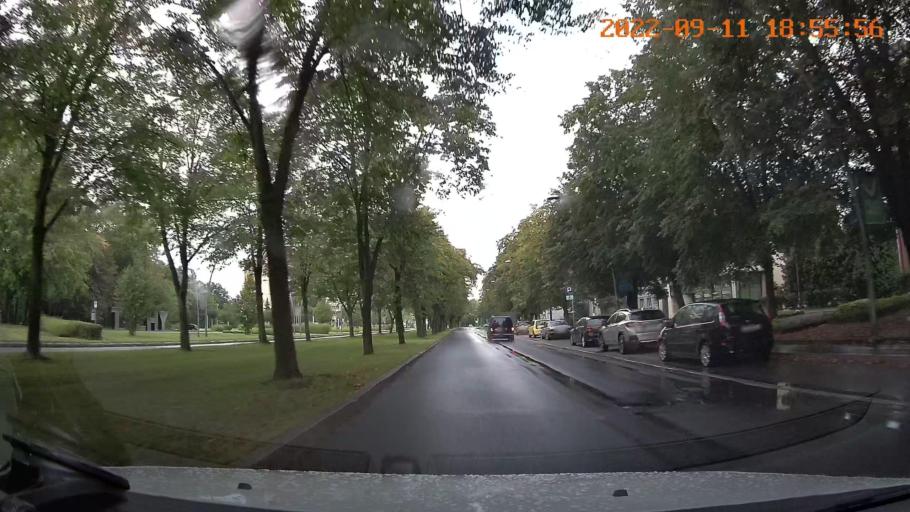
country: PL
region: Silesian Voivodeship
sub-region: Tychy
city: Tychy
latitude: 50.1152
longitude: 18.9939
